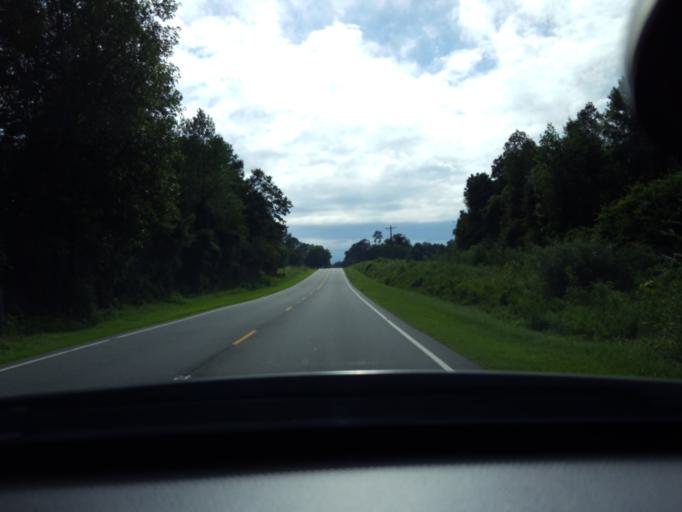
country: US
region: North Carolina
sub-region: Duplin County
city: Kenansville
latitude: 35.0095
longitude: -77.8985
